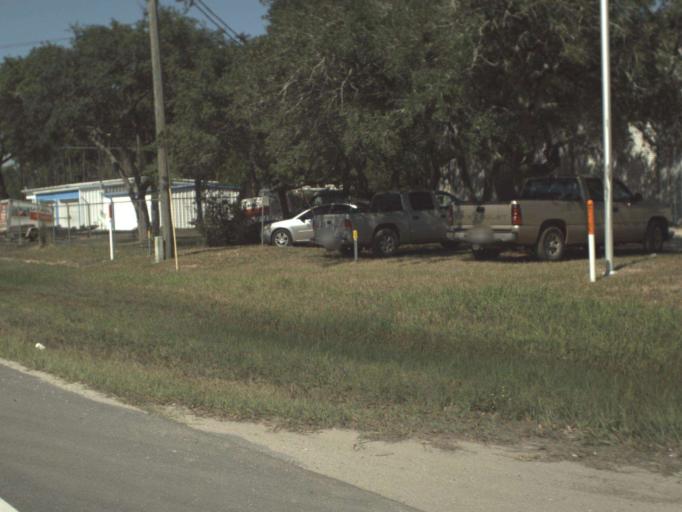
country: US
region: Florida
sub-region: Walton County
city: Miramar Beach
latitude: 30.4631
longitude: -86.3881
